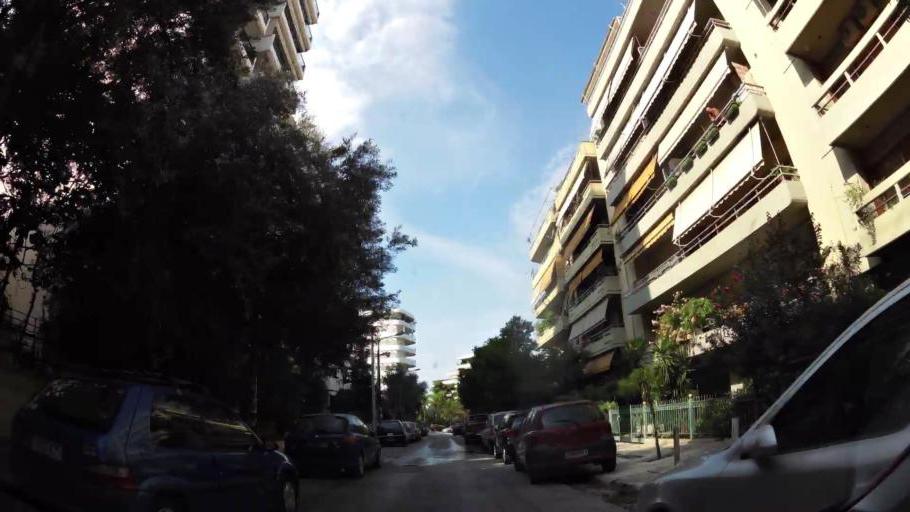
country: GR
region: Attica
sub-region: Nomarchia Athinas
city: Nea Smyrni
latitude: 37.9476
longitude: 23.7096
